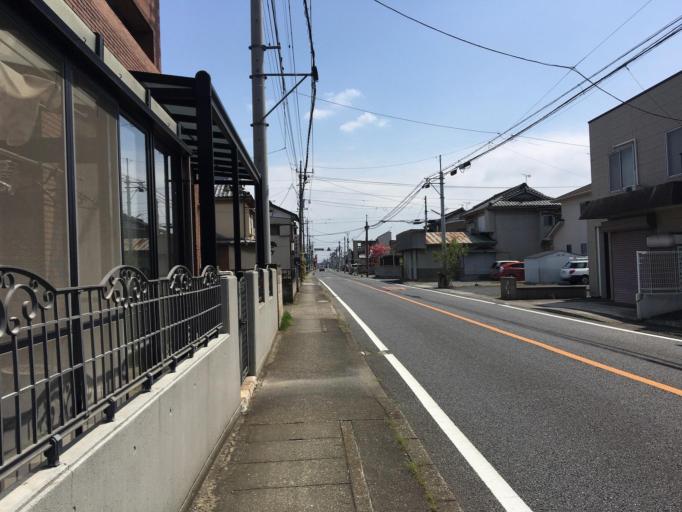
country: JP
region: Gunma
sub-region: Sawa-gun
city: Tamamura
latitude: 36.3033
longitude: 139.1055
